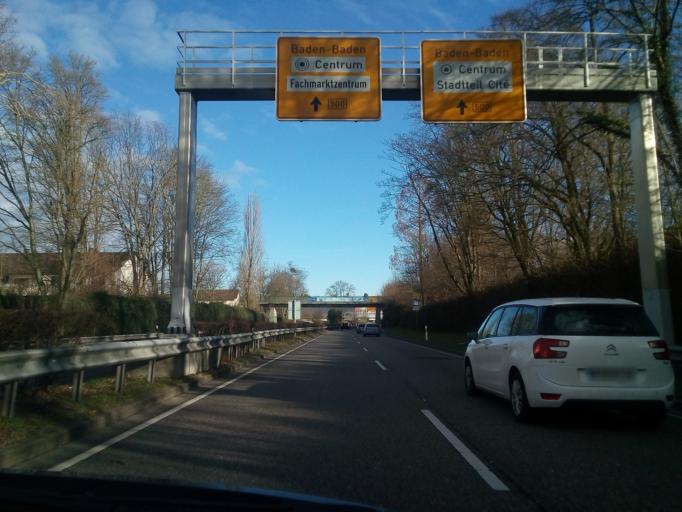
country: DE
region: Baden-Wuerttemberg
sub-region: Karlsruhe Region
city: Sinzheim
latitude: 48.7801
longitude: 8.1899
